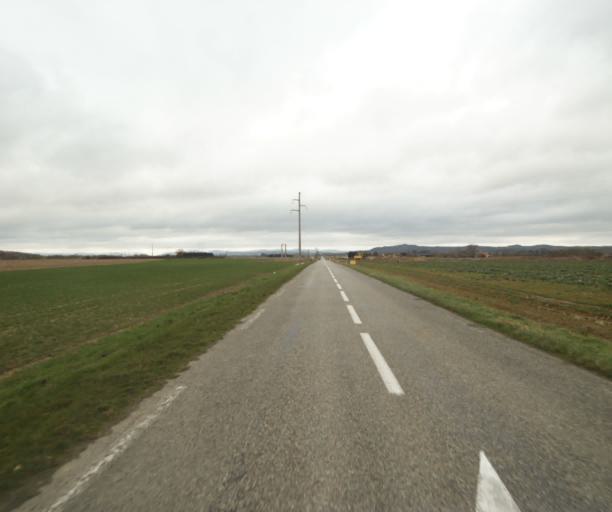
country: FR
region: Midi-Pyrenees
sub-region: Departement de l'Ariege
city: Mazeres
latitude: 43.2153
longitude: 1.6326
